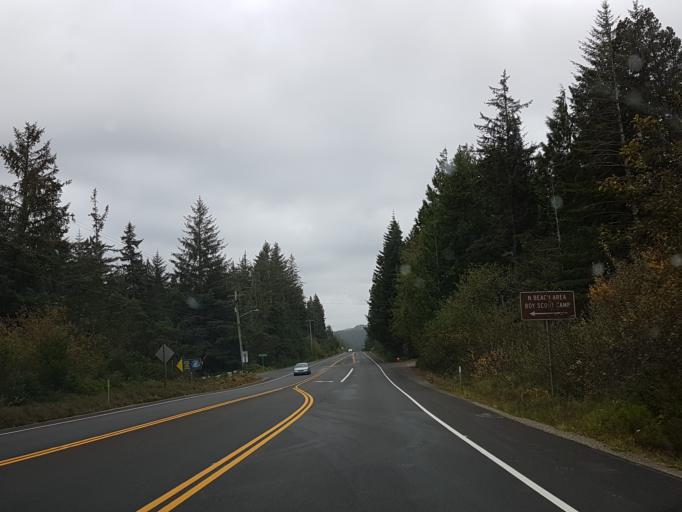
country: US
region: Oregon
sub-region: Lane County
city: Dunes City
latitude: 43.8963
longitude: -124.1177
